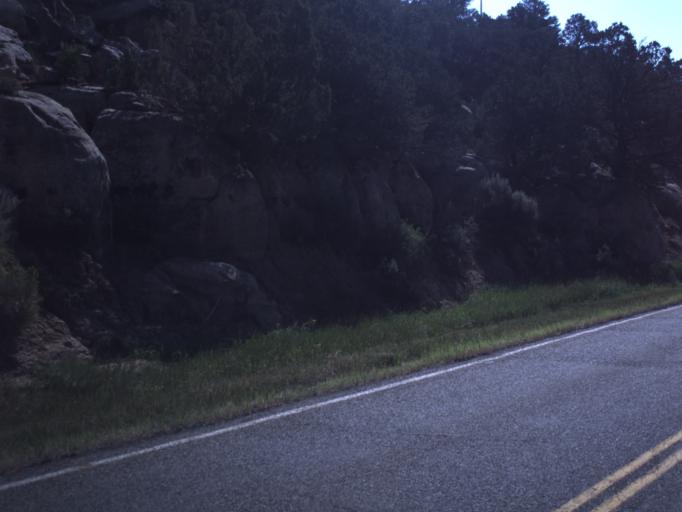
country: US
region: Utah
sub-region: Duchesne County
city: Duchesne
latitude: 40.3248
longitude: -110.6617
